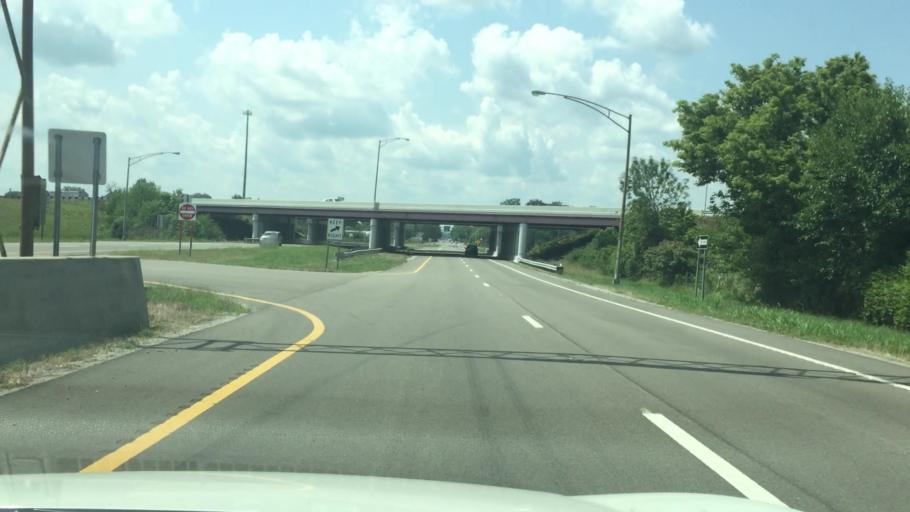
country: US
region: Ohio
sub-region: Clark County
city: Lisbon
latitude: 39.9240
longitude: -83.6860
